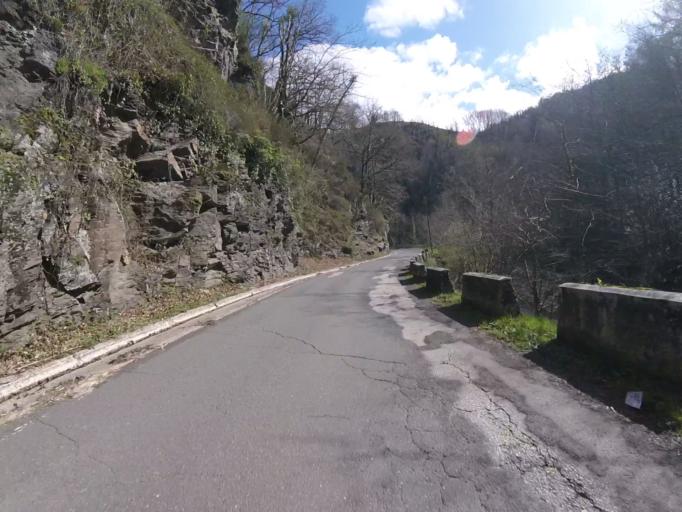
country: ES
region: Navarre
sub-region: Provincia de Navarra
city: Goizueta
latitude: 43.1400
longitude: -1.8467
